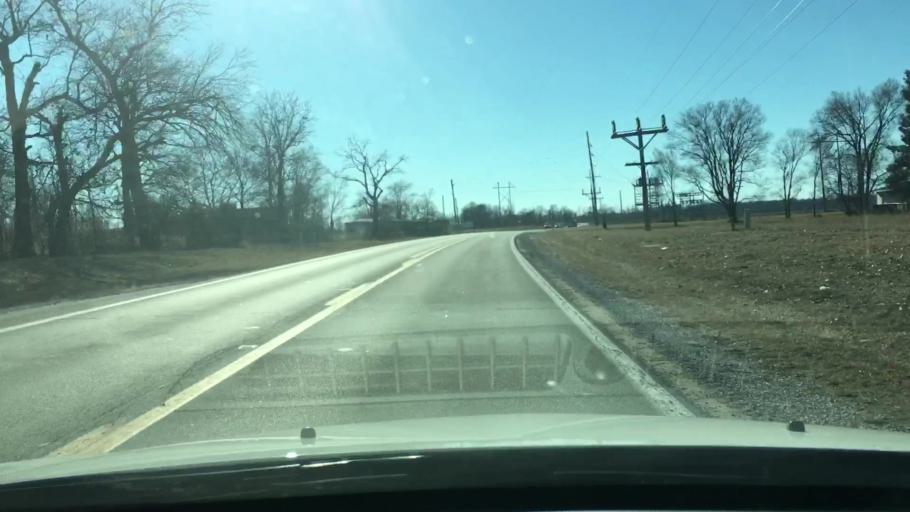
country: US
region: Illinois
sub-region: Cass County
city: Beardstown
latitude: 39.9429
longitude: -90.4877
